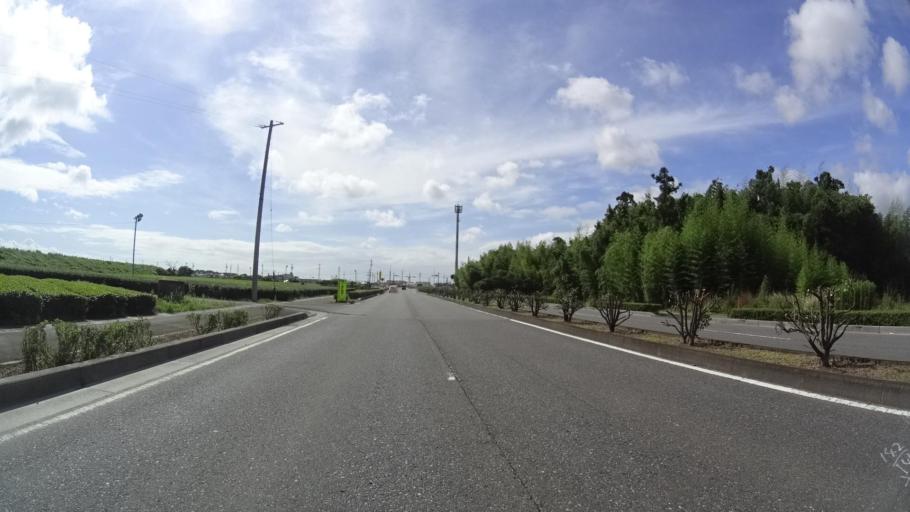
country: JP
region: Mie
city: Kameyama
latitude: 34.8965
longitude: 136.5050
